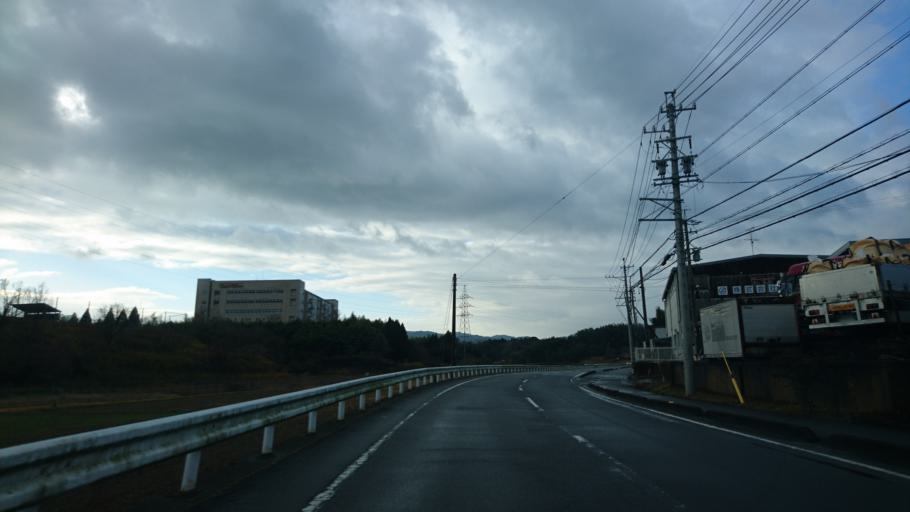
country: JP
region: Mie
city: Ueno-ebisumachi
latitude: 34.7219
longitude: 136.0800
